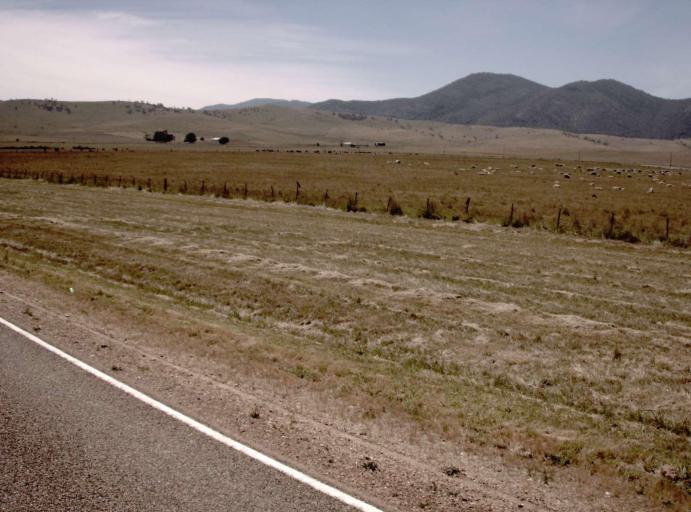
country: AU
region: Victoria
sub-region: Alpine
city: Mount Beauty
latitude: -37.0019
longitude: 147.6695
